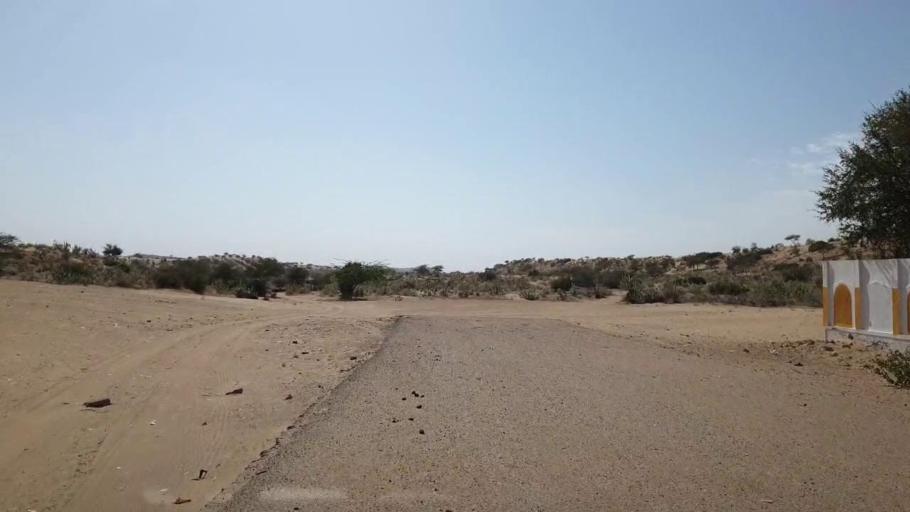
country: PK
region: Sindh
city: Umarkot
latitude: 25.1616
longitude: 70.0301
